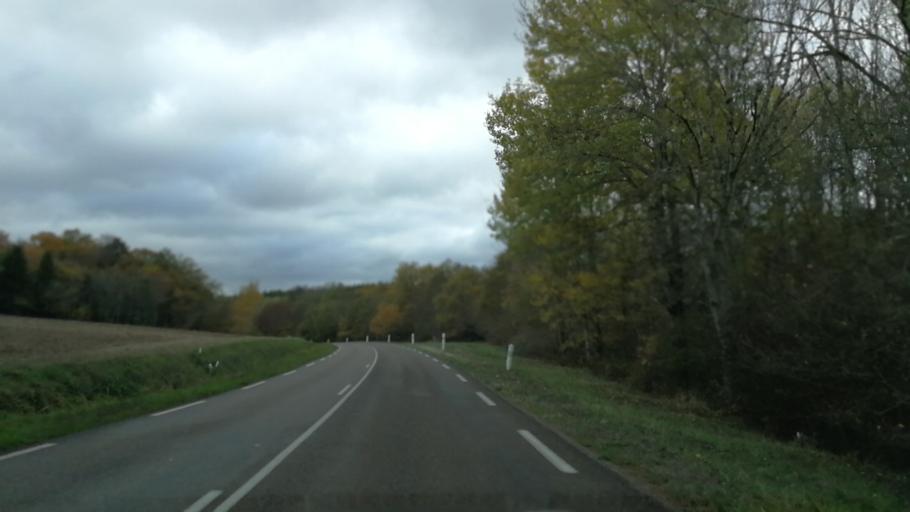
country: FR
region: Bourgogne
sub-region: Departement de la Cote-d'Or
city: Saulieu
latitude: 47.2595
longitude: 4.3197
